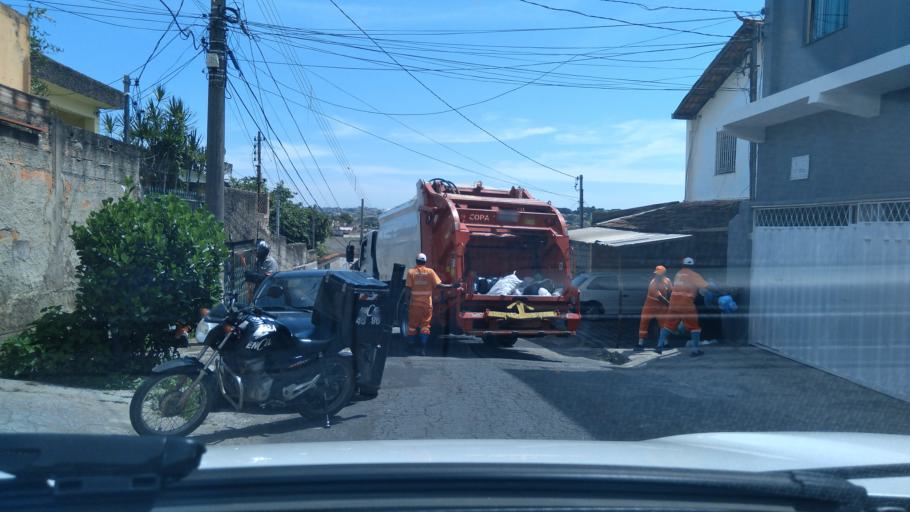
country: BR
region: Minas Gerais
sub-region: Contagem
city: Contagem
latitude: -19.9264
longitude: -44.0040
